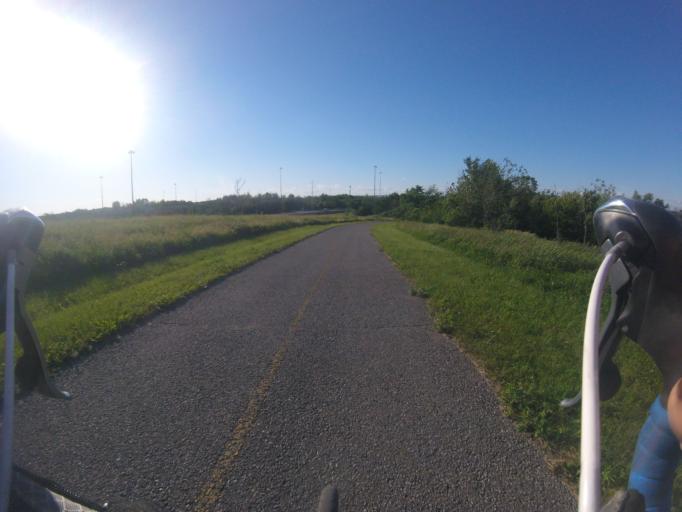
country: CA
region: Ontario
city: Bells Corners
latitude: 45.3398
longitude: -75.8132
